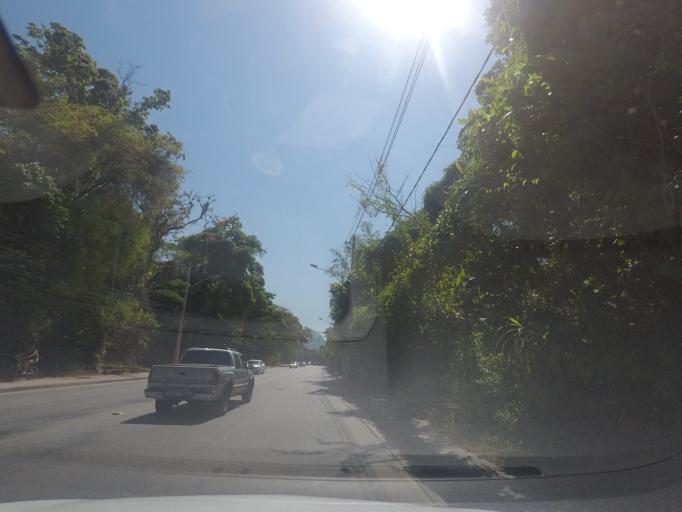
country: BR
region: Rio de Janeiro
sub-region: Nilopolis
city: Nilopolis
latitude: -22.9874
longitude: -43.4792
